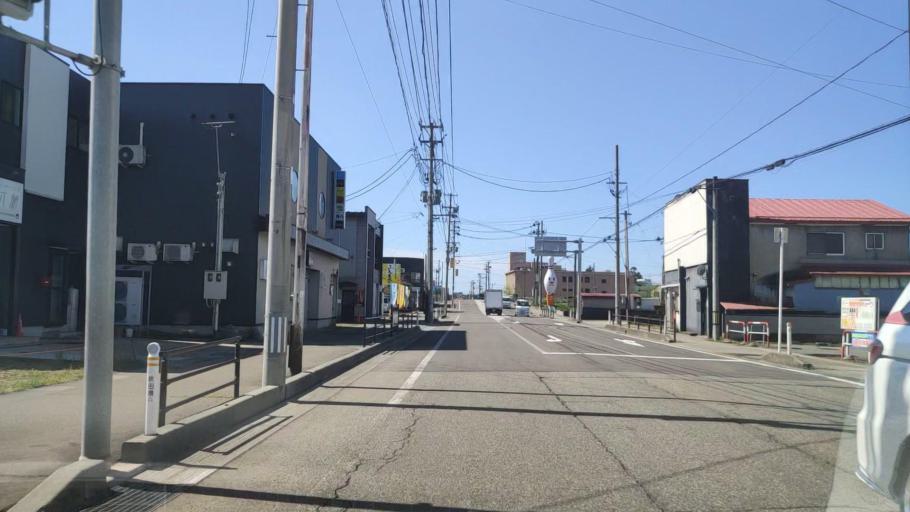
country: JP
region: Akita
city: Omagari
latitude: 39.4623
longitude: 140.4762
